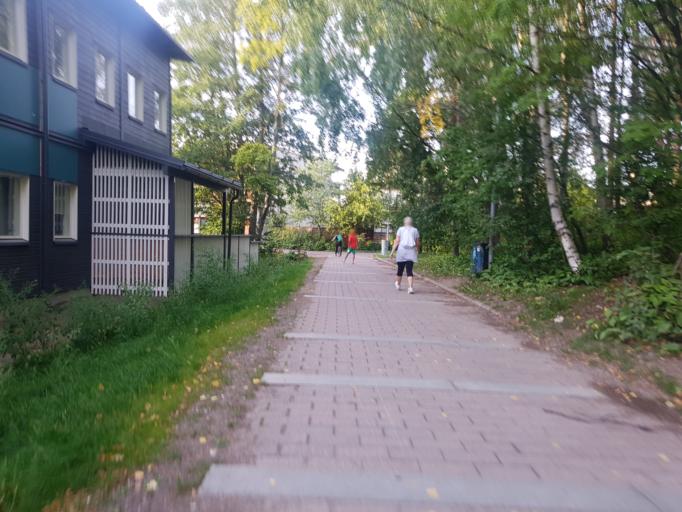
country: FI
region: Uusimaa
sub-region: Helsinki
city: Teekkarikylae
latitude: 60.2458
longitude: 24.8612
